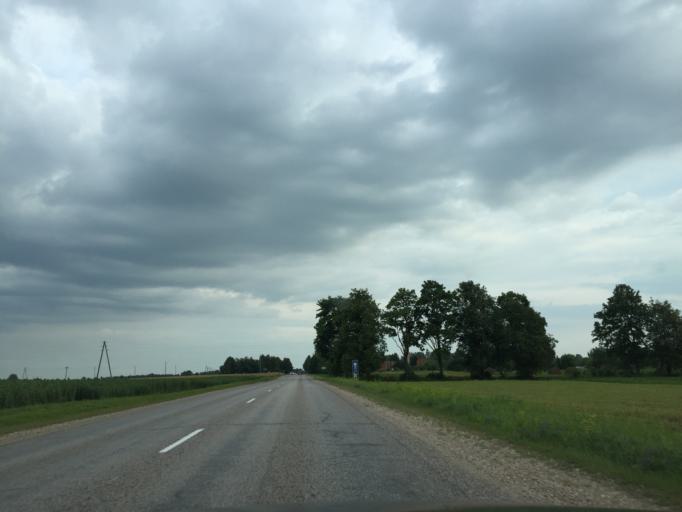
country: LV
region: Dobeles Rajons
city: Dobele
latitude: 56.5710
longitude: 23.2991
